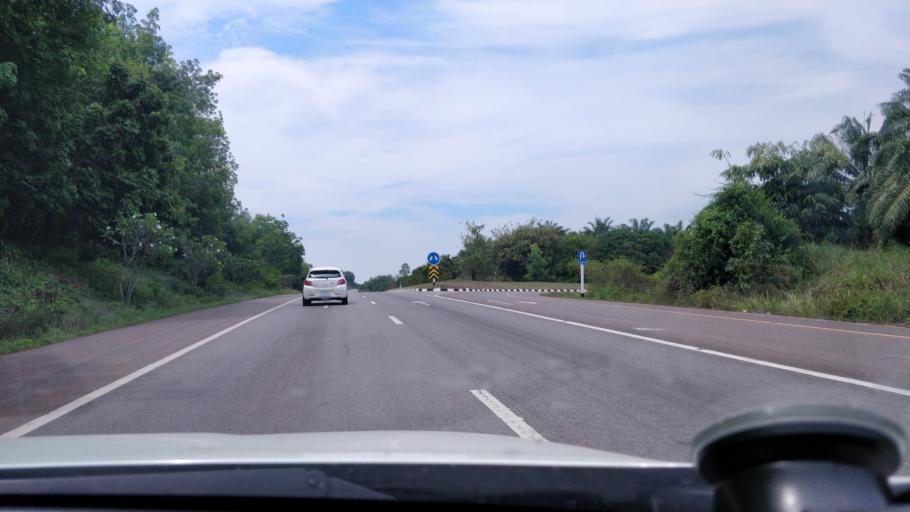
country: TH
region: Surat Thani
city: Khian Sa
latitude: 8.7901
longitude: 99.1615
